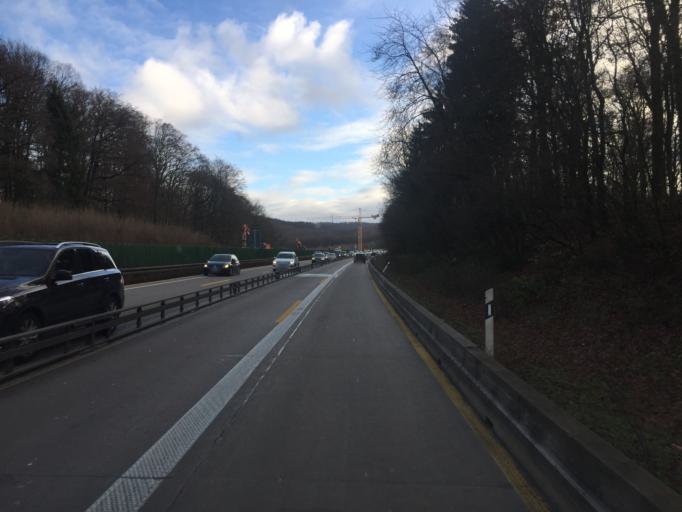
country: DE
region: Lower Saxony
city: Holle
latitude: 52.1199
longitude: 10.1130
